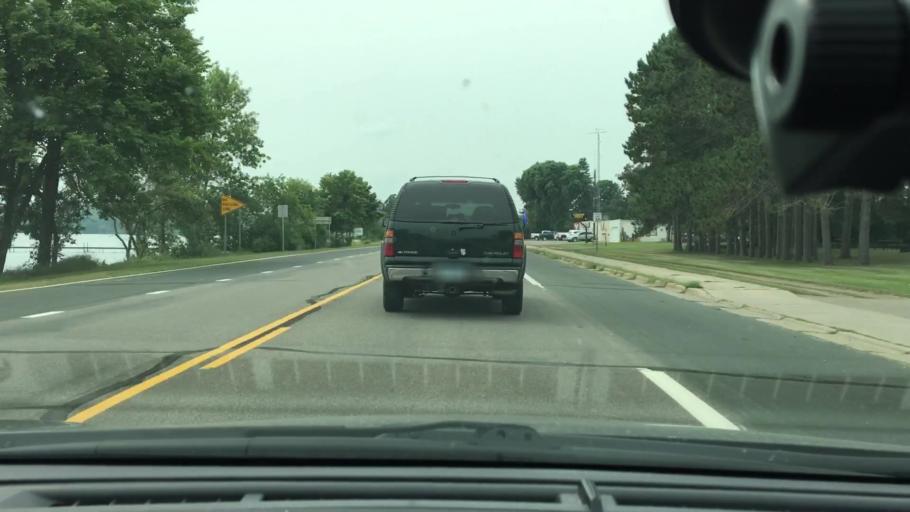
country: US
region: Minnesota
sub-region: Mille Lacs County
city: Vineland
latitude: 46.2989
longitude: -93.8215
